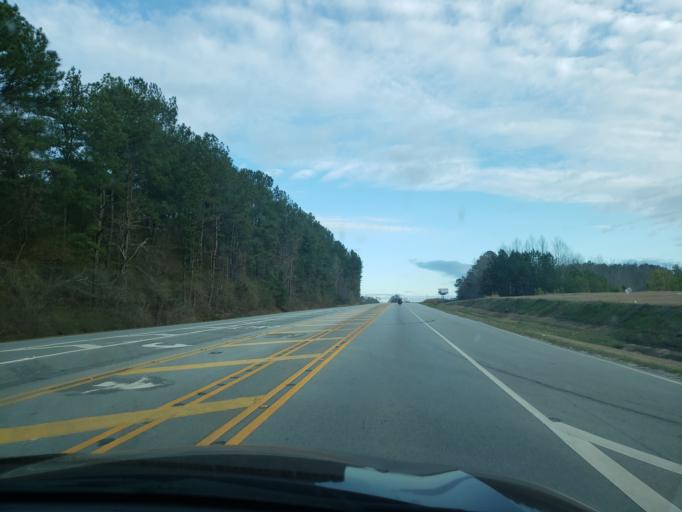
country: US
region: Alabama
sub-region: Randolph County
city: Wedowee
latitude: 33.3155
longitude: -85.4847
